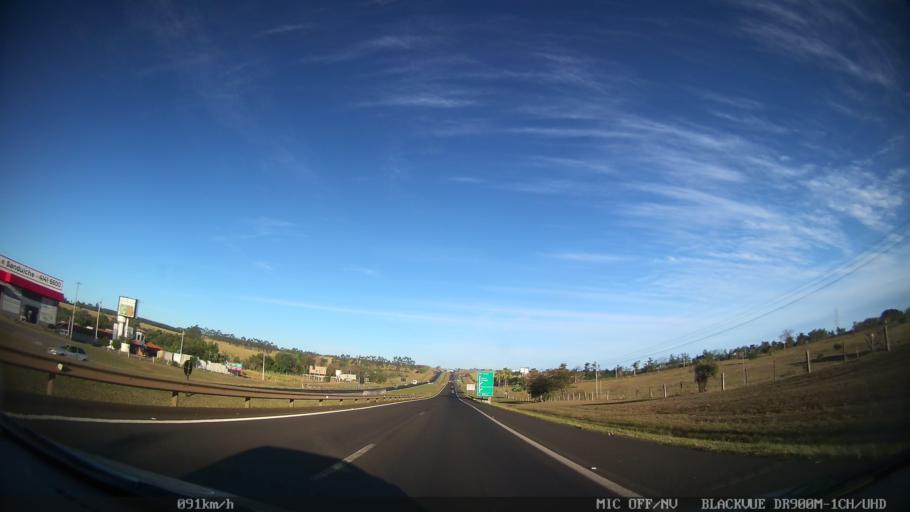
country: BR
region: Sao Paulo
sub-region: Sao Jose Do Rio Preto
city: Sao Jose do Rio Preto
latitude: -20.8991
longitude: -49.3011
